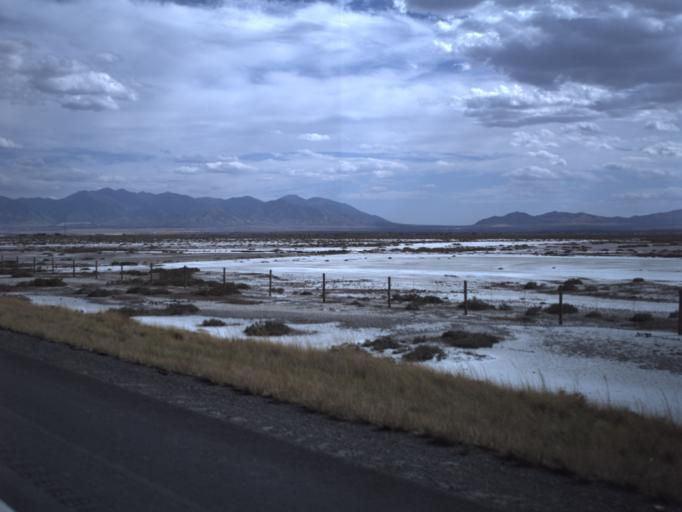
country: US
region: Utah
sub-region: Tooele County
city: Grantsville
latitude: 40.6977
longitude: -112.4812
